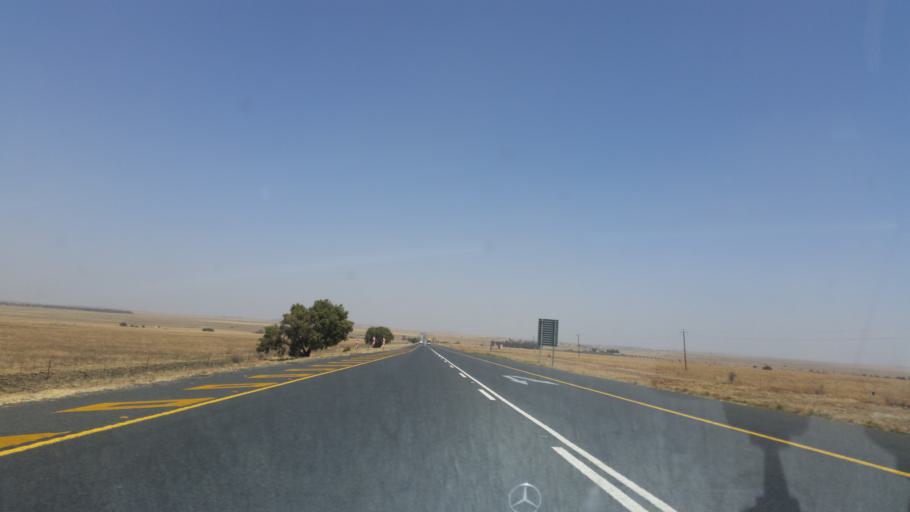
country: ZA
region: Orange Free State
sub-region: Lejweleputswa District Municipality
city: Winburg
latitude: -28.7180
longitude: 26.7742
